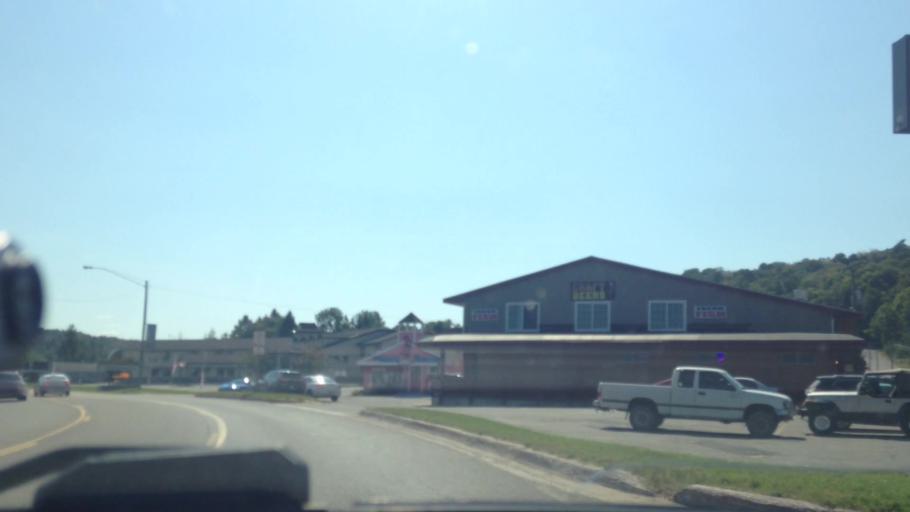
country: US
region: Michigan
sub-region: Alger County
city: Munising
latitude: 46.4076
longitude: -86.6512
